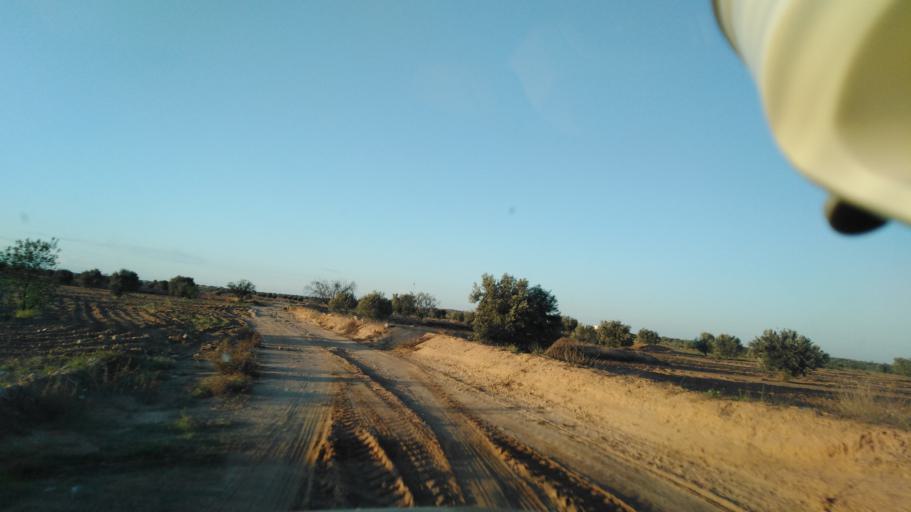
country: TN
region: Safaqis
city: Bi'r `Ali Bin Khalifah
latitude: 34.6723
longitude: 10.3838
